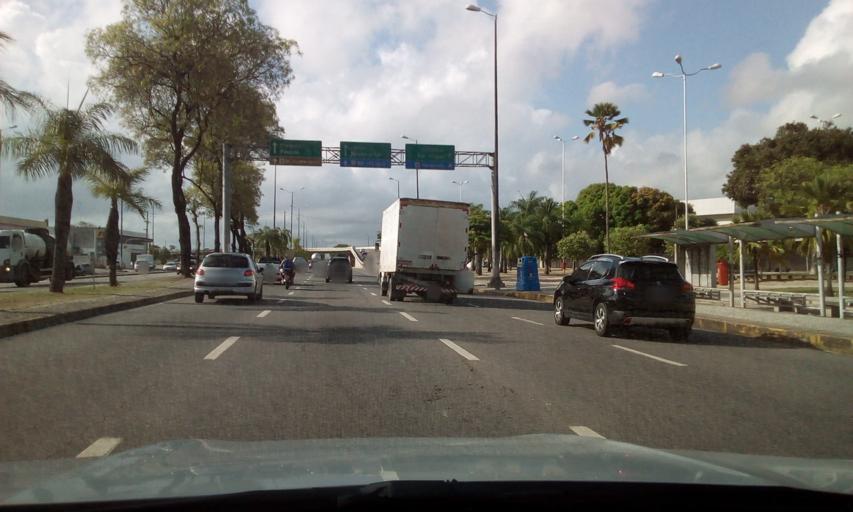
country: BR
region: Pernambuco
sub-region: Recife
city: Recife
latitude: -8.1336
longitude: -34.9166
